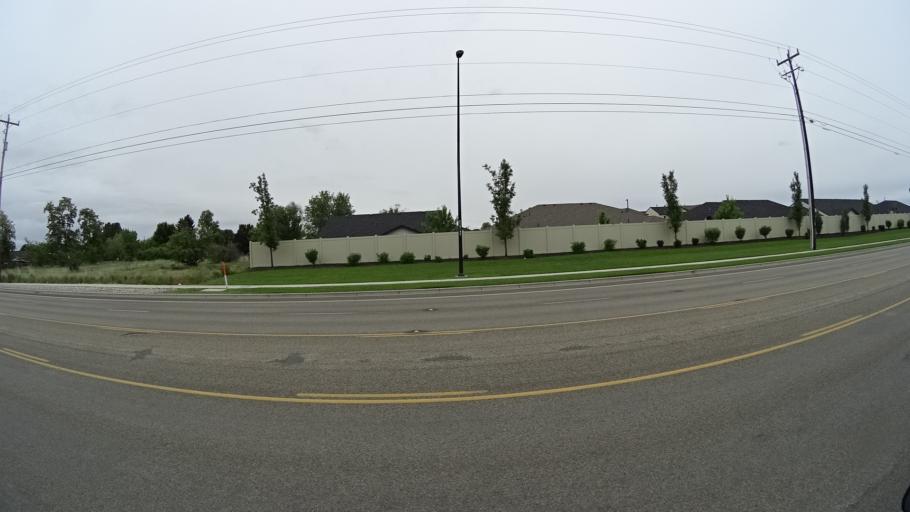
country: US
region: Idaho
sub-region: Ada County
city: Meridian
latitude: 43.6339
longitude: -116.3661
